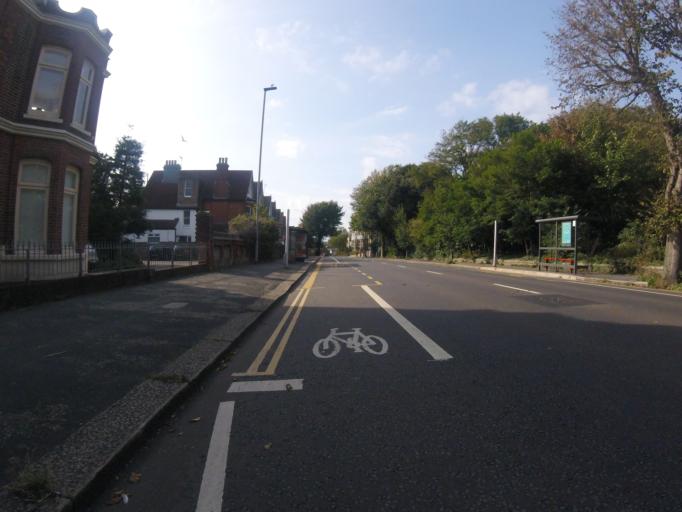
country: GB
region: England
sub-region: Brighton and Hove
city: Hove
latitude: 50.8384
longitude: -0.1693
